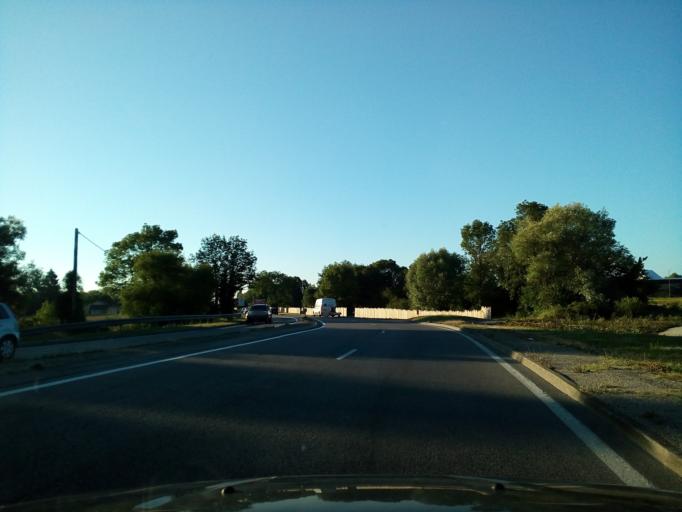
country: FR
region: Rhone-Alpes
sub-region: Departement de l'Isere
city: La Verpilliere
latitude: 45.6291
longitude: 5.1579
